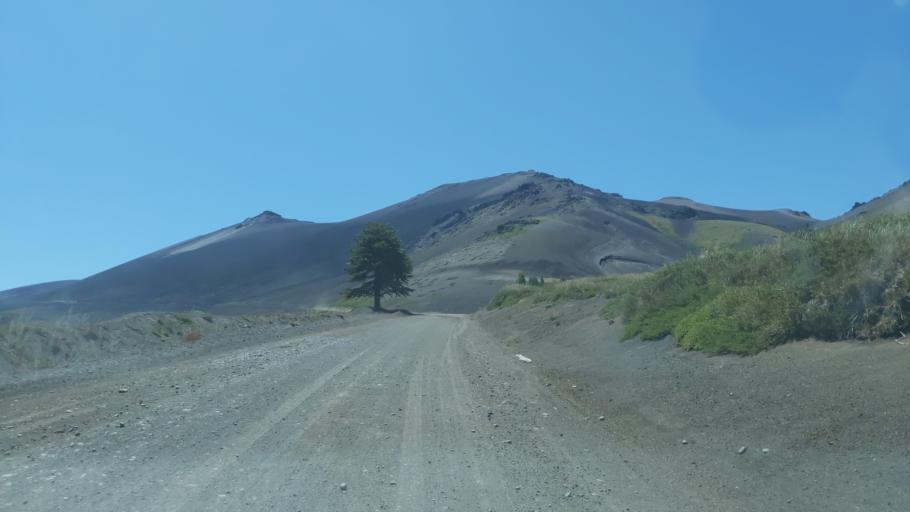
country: CL
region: Araucania
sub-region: Provincia de Cautin
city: Vilcun
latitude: -38.4173
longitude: -71.5438
